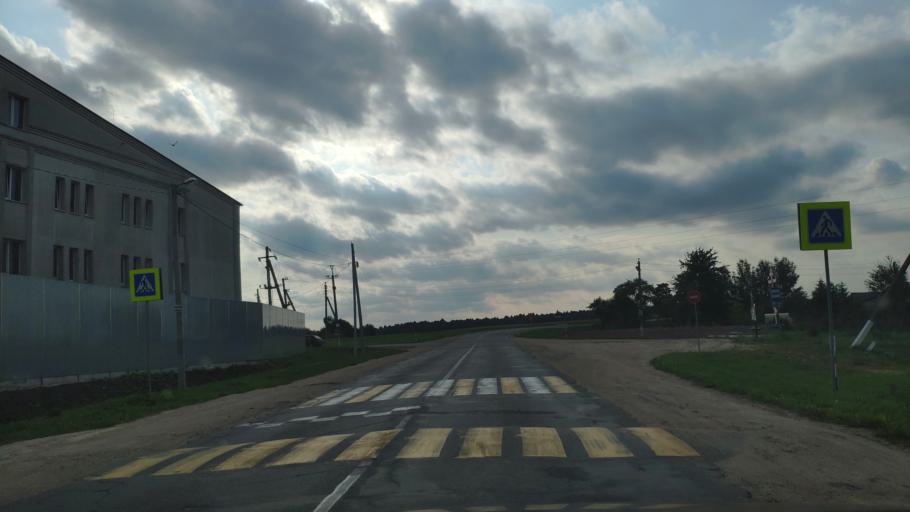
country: BY
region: Minsk
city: Khatsyezhyna
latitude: 53.8317
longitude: 27.3089
